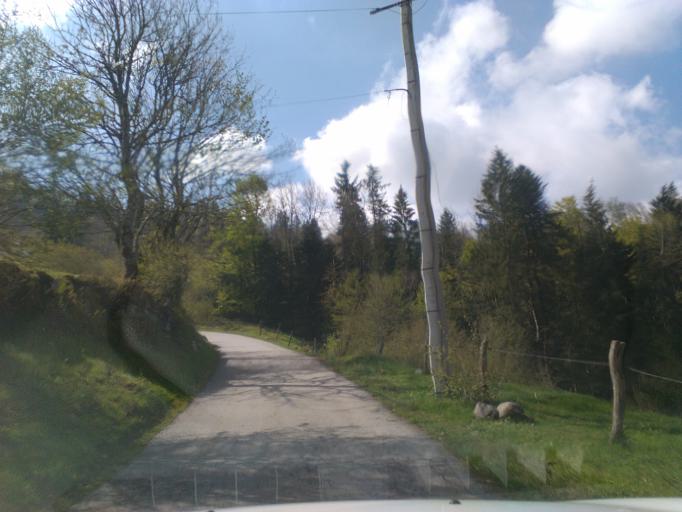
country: FR
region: Lorraine
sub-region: Departement des Vosges
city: Cornimont
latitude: 47.9867
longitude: 6.7993
